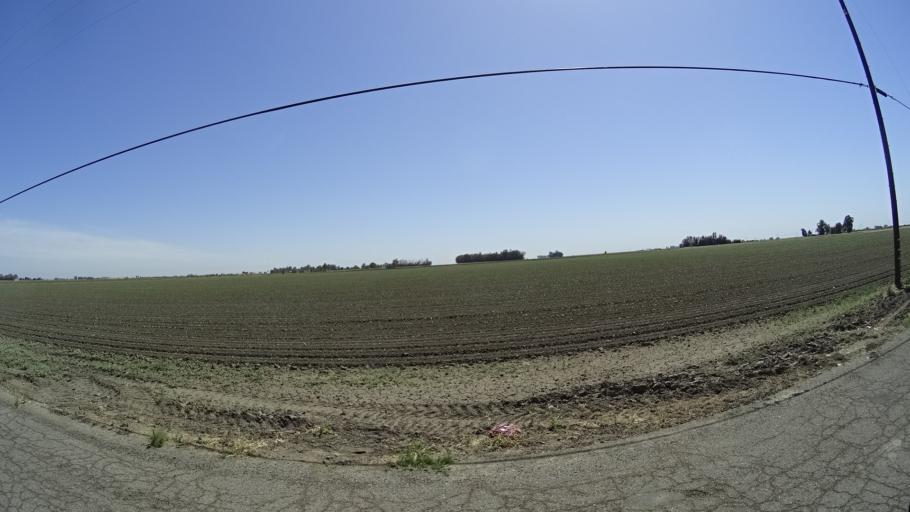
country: US
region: California
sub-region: Kings County
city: Stratford
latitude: 36.1950
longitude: -119.8161
